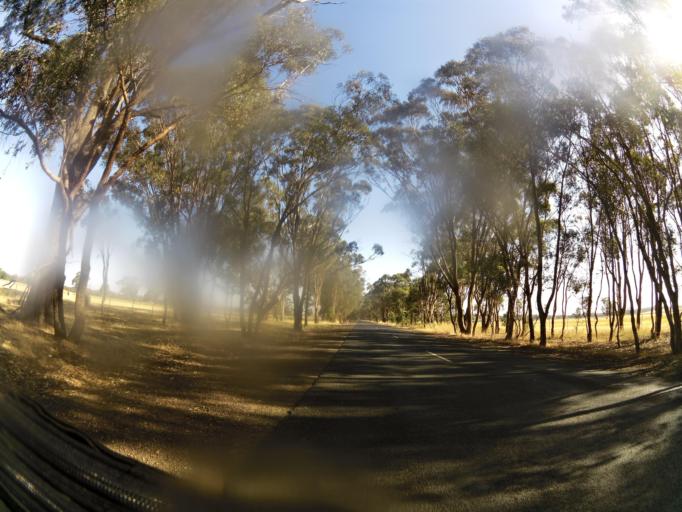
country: AU
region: Victoria
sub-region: Murrindindi
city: Kinglake West
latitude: -36.9742
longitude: 145.1098
